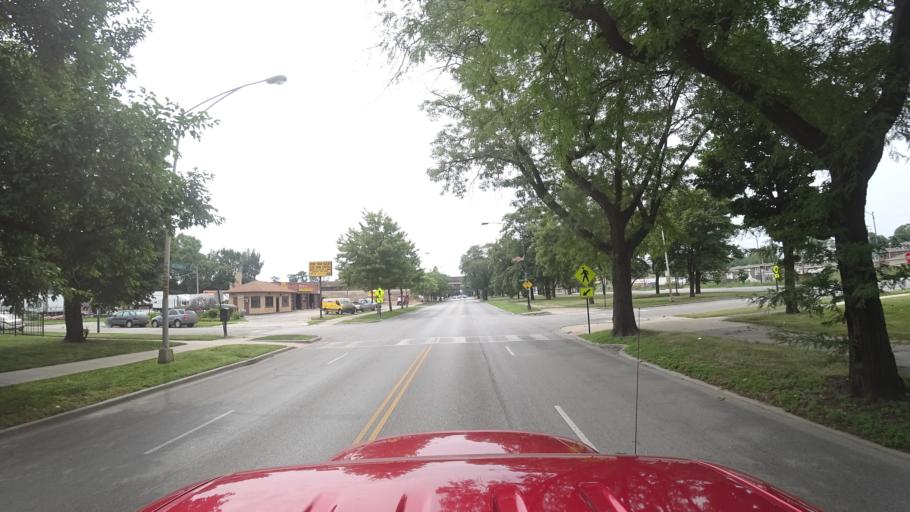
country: US
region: Illinois
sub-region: Cook County
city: Chicago
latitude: 41.8288
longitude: -87.6844
